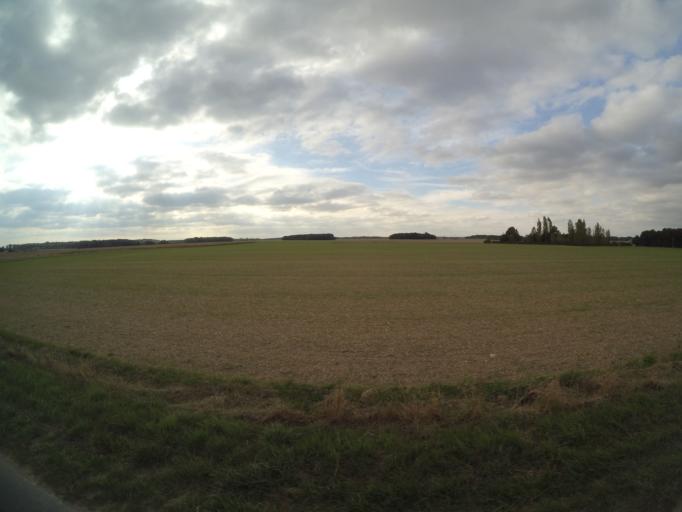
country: FR
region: Centre
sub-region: Departement d'Indre-et-Loire
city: Nazelles-Negron
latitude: 47.4768
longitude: 0.9430
